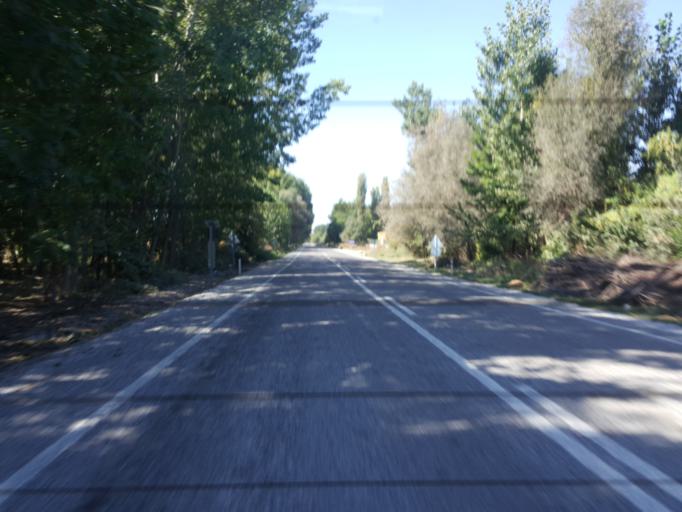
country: TR
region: Tokat
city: Pazar
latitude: 40.2701
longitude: 36.2398
